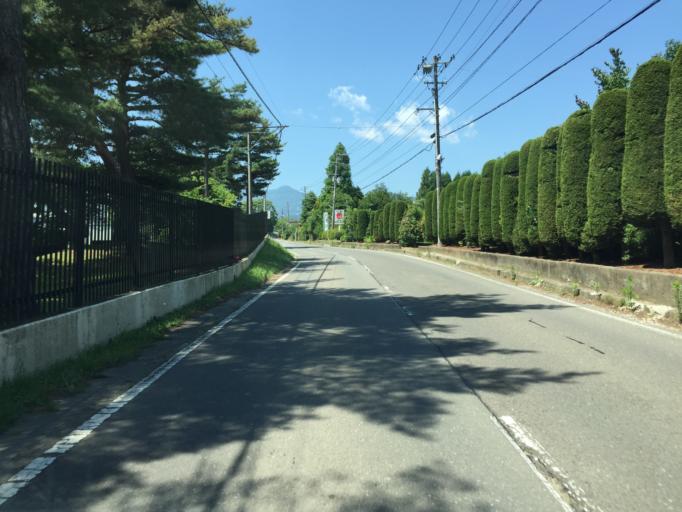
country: JP
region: Fukushima
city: Fukushima-shi
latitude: 37.7128
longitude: 140.3809
